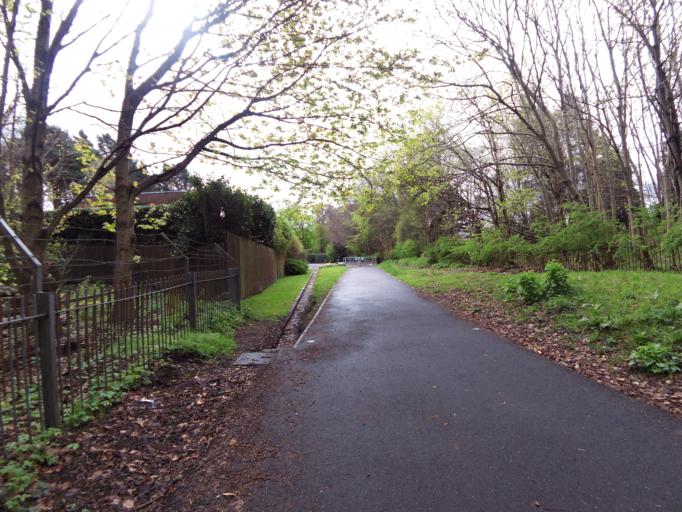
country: GB
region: Scotland
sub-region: Edinburgh
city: Colinton
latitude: 55.9666
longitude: -3.2939
